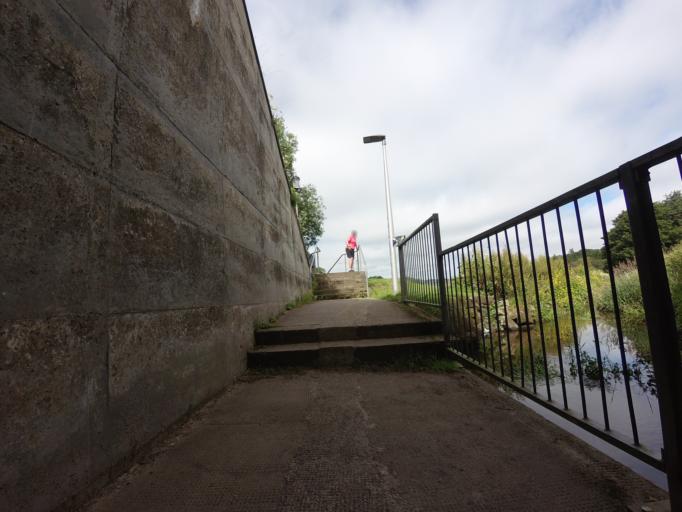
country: GB
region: Scotland
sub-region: Aberdeenshire
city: Turriff
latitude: 57.5345
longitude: -2.4621
